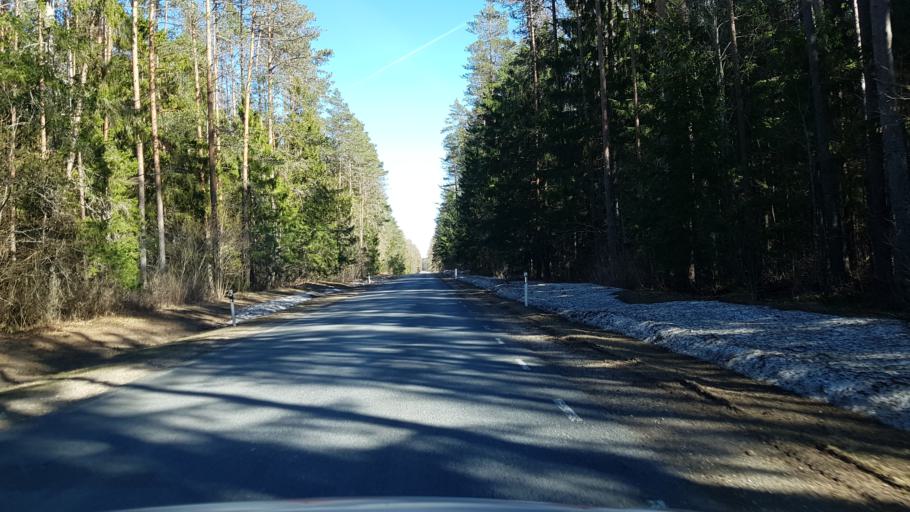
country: EE
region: Laeaene-Virumaa
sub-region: Vinni vald
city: Vinni
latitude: 59.2738
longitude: 26.6231
